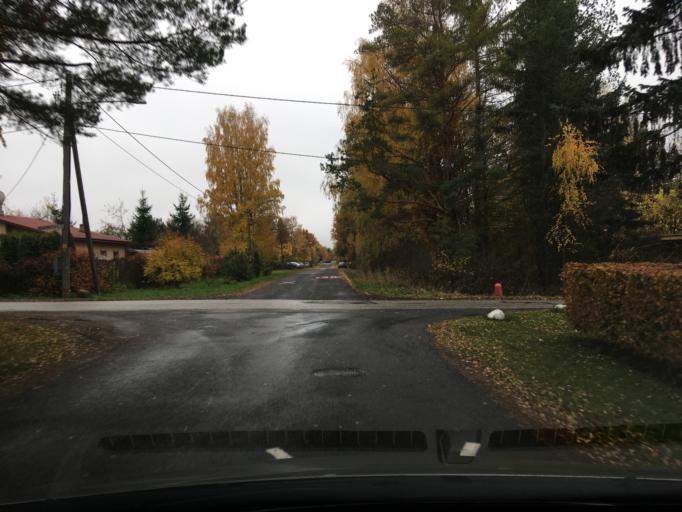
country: EE
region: Tartu
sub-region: Tartu linn
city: Tartu
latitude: 58.3507
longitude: 26.7784
